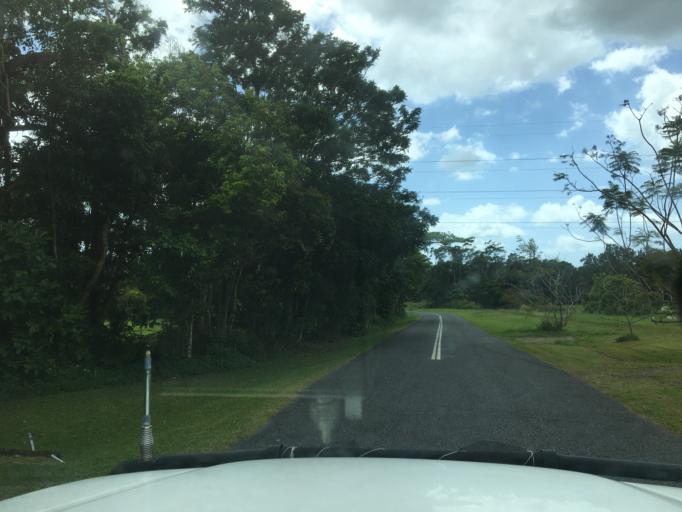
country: AU
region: Queensland
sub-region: Cairns
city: Woree
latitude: -17.2180
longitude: 145.9160
